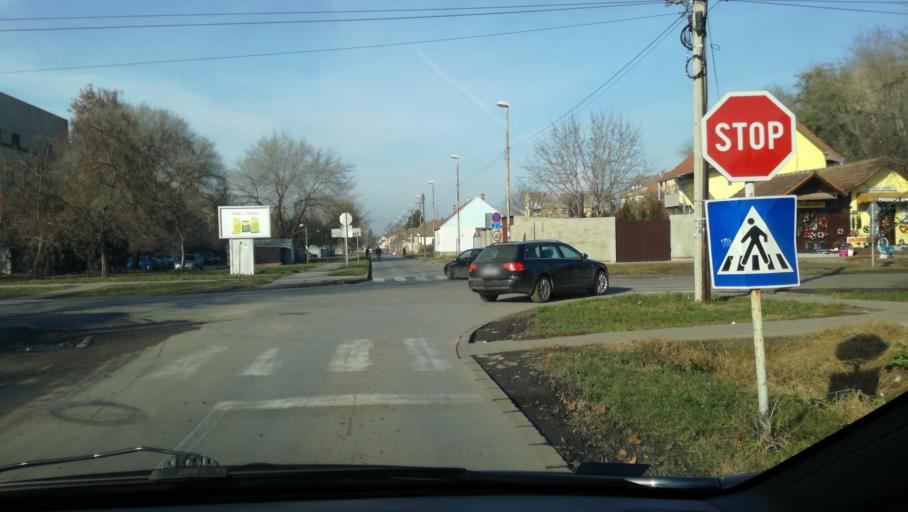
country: RS
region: Autonomna Pokrajina Vojvodina
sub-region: Severnobanatski Okrug
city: Kikinda
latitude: 45.8172
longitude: 20.4514
